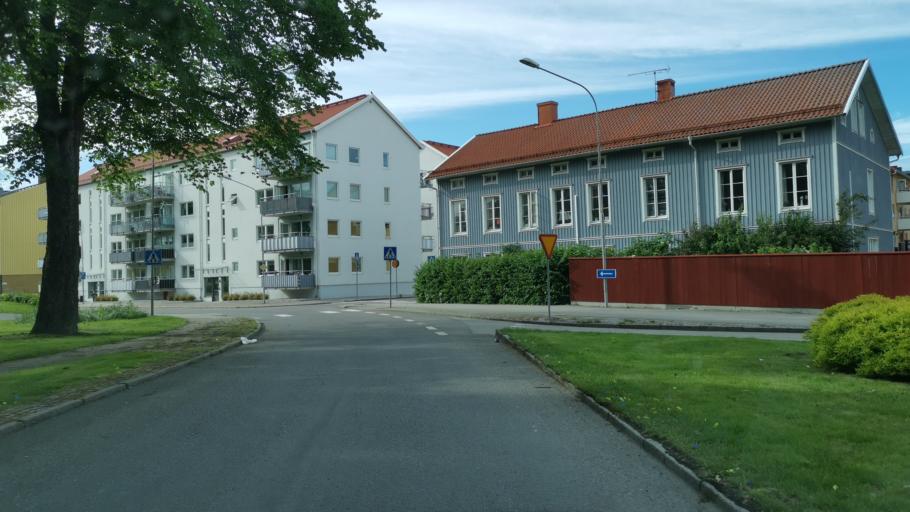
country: SE
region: Vaestra Goetaland
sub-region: Vanersborgs Kommun
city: Vanersborg
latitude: 58.3801
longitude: 12.3299
